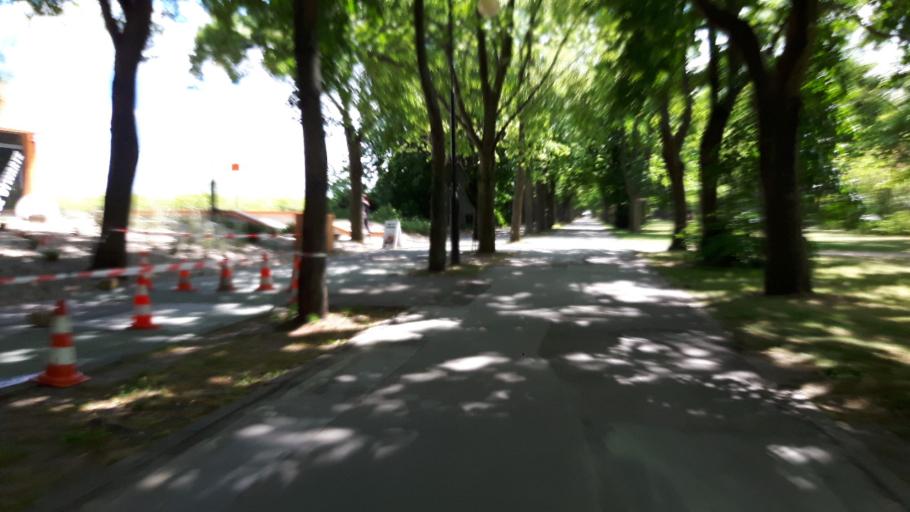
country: PL
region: Pomeranian Voivodeship
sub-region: Sopot
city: Sopot
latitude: 54.4519
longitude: 18.5650
